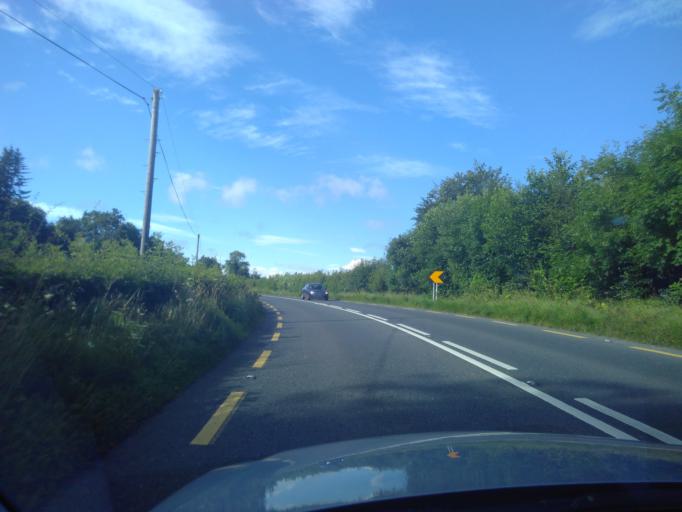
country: IE
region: Ulster
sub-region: County Donegal
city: Ballybofey
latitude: 54.8293
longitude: -7.7476
